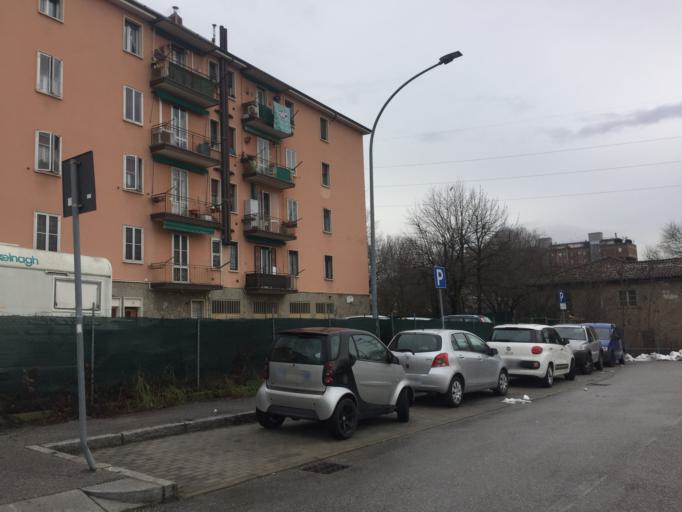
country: IT
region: Emilia-Romagna
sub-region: Provincia di Bologna
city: Casalecchio di Reno
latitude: 44.5070
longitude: 11.2930
